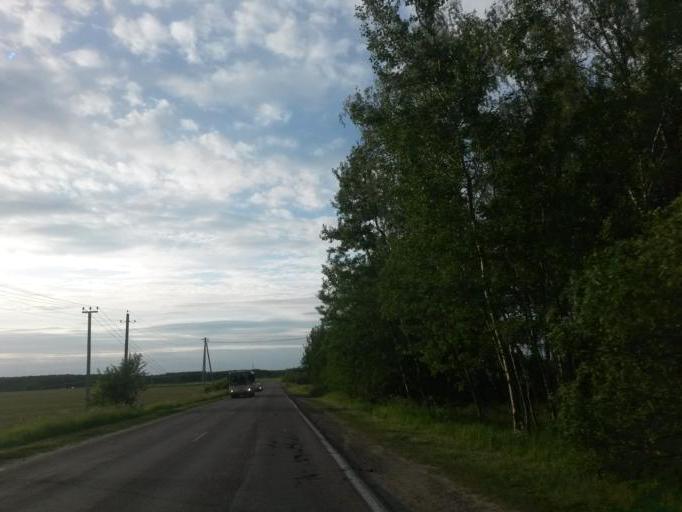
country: RU
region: Moskovskaya
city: Melikhovo
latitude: 55.1900
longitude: 37.7016
